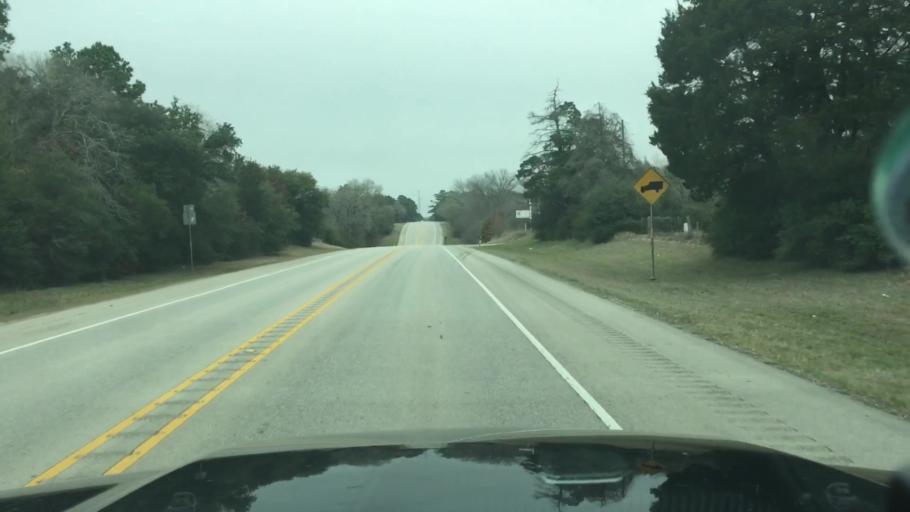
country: US
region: Texas
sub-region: Fayette County
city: La Grange
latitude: 30.0025
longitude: -96.8926
